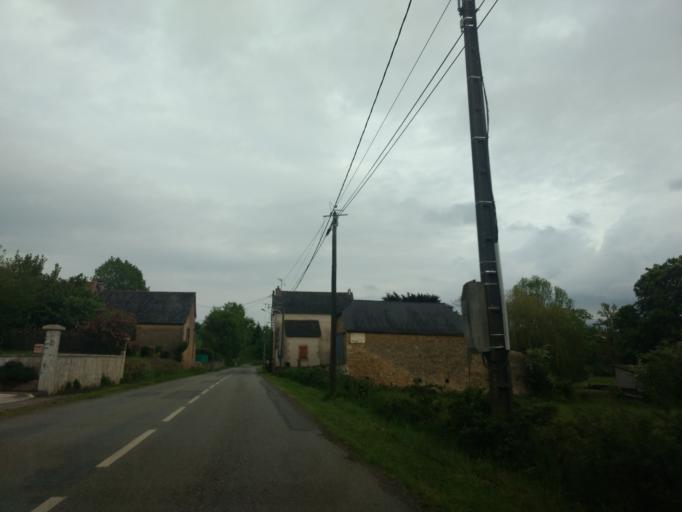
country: FR
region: Midi-Pyrenees
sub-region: Departement de l'Aveyron
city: Montbazens
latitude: 44.4864
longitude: 2.2224
